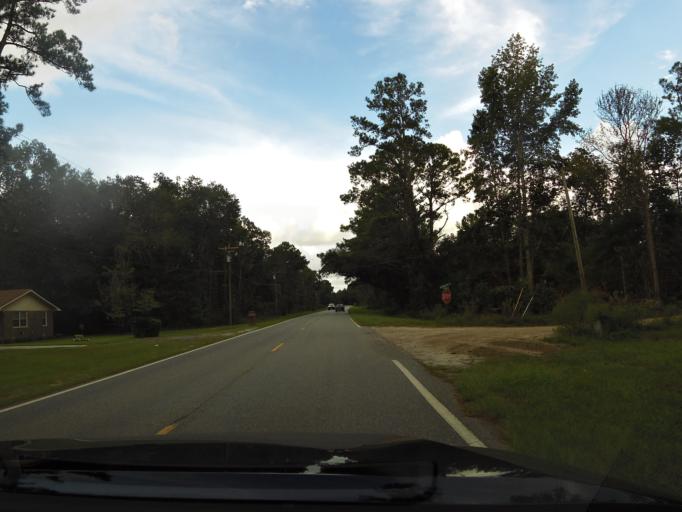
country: US
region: Georgia
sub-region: Liberty County
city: Midway
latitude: 31.8473
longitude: -81.4183
